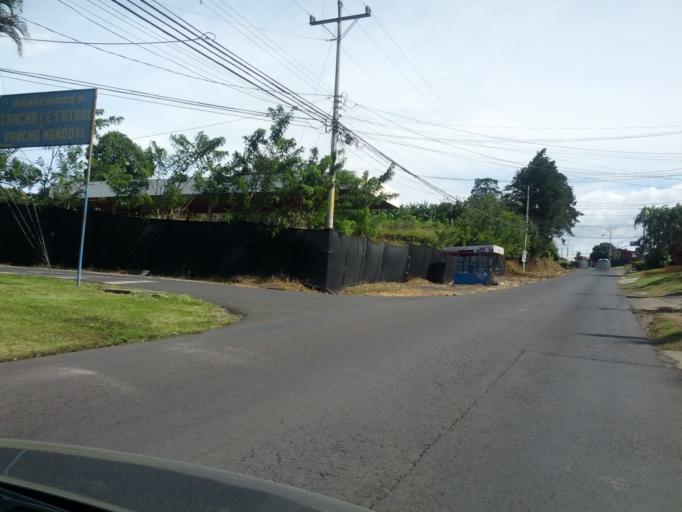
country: CR
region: Alajuela
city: Alajuela
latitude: 10.0270
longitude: -84.1818
